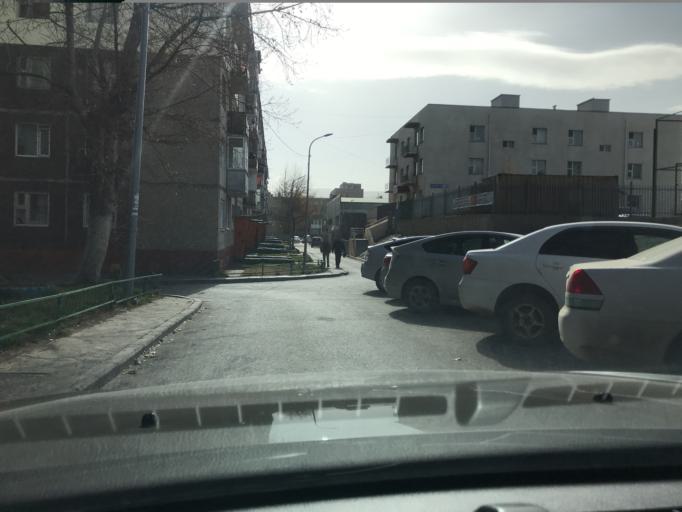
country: MN
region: Ulaanbaatar
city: Ulaanbaatar
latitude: 47.9206
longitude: 106.9520
